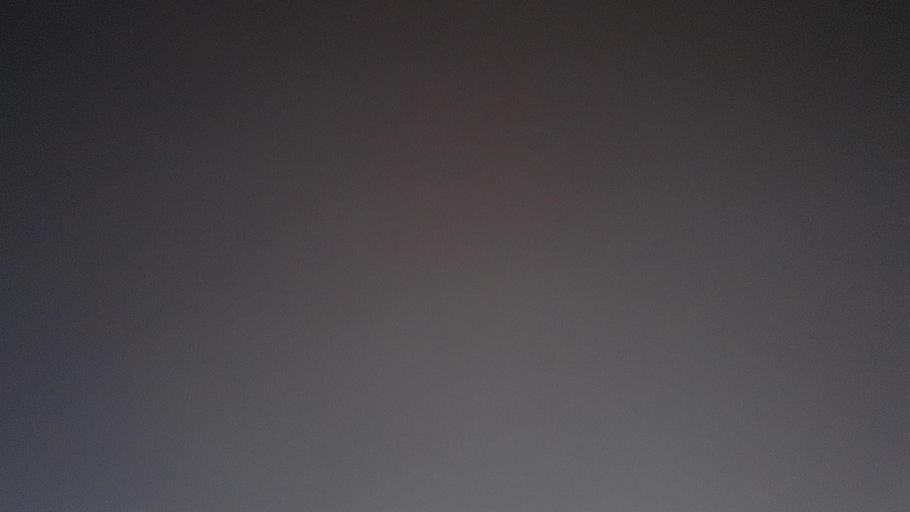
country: FI
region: Lapland
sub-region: Torniolaakso
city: Ylitornio
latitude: 66.2093
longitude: 23.6951
